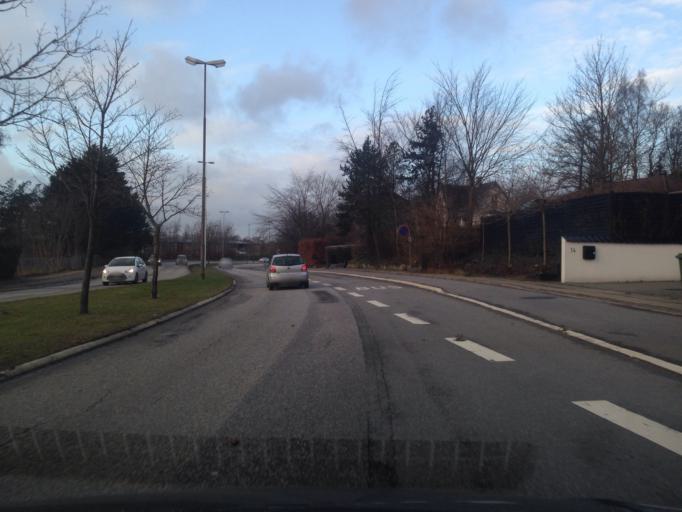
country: DK
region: Capital Region
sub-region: Rudersdal Kommune
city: Birkerod
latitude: 55.8434
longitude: 12.4394
